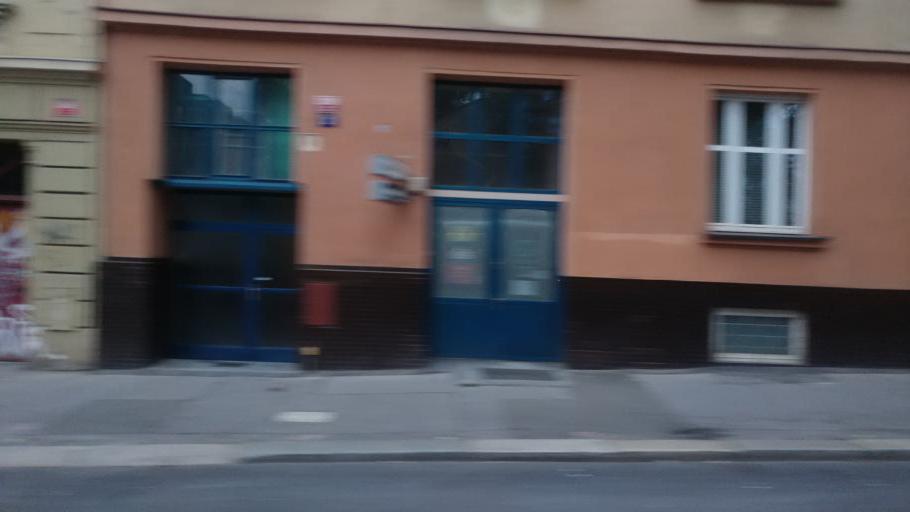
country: CZ
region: Praha
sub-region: Praha 8
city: Liben
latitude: 50.1039
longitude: 14.4794
